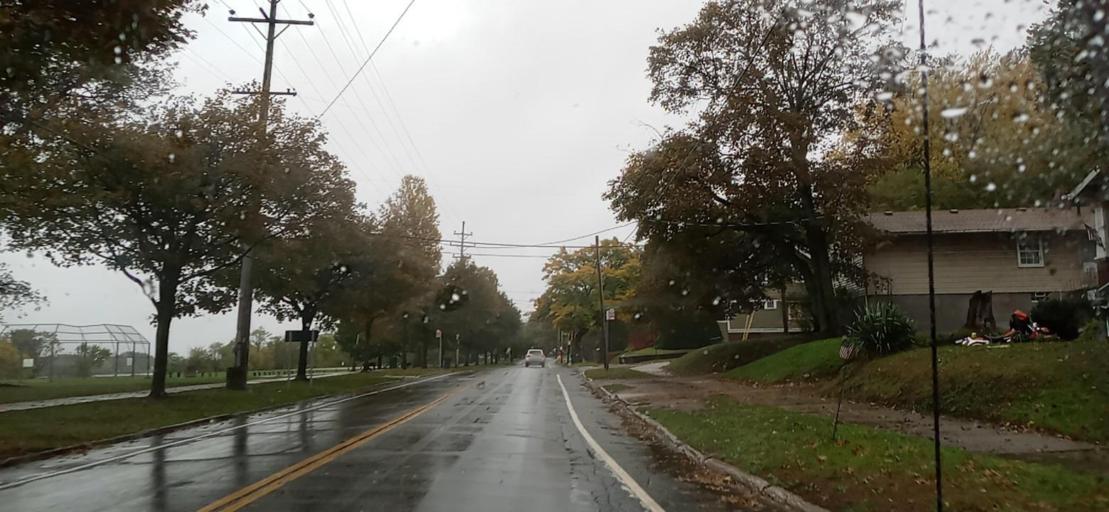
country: US
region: Ohio
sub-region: Summit County
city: Akron
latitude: 41.0603
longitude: -81.5505
